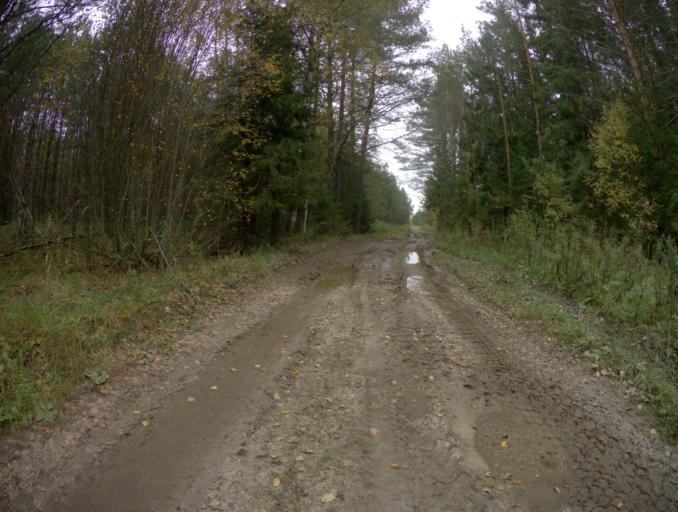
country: RU
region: Vladimir
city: Stepantsevo
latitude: 56.3138
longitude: 41.5928
